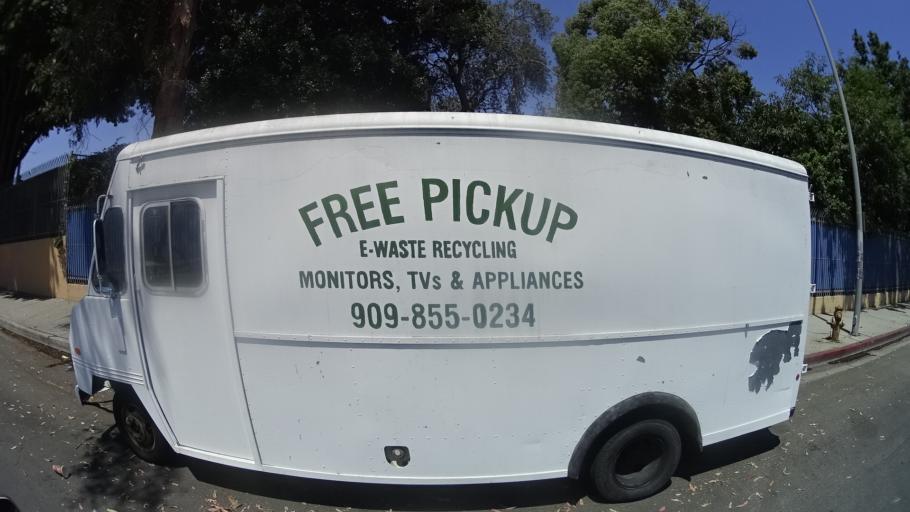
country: US
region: California
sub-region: Los Angeles County
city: View Park-Windsor Hills
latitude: 33.9977
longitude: -118.3259
